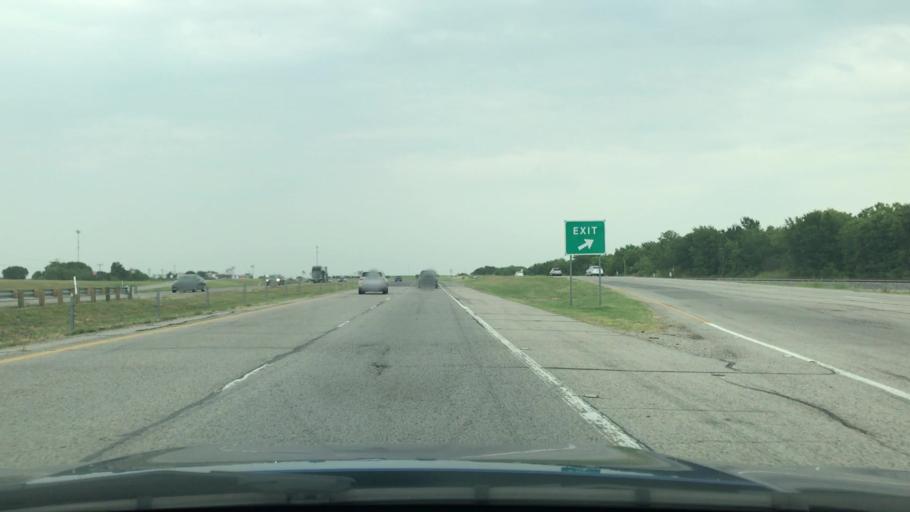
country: US
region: Texas
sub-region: Kaufman County
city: Talty
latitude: 32.7392
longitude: -96.3723
